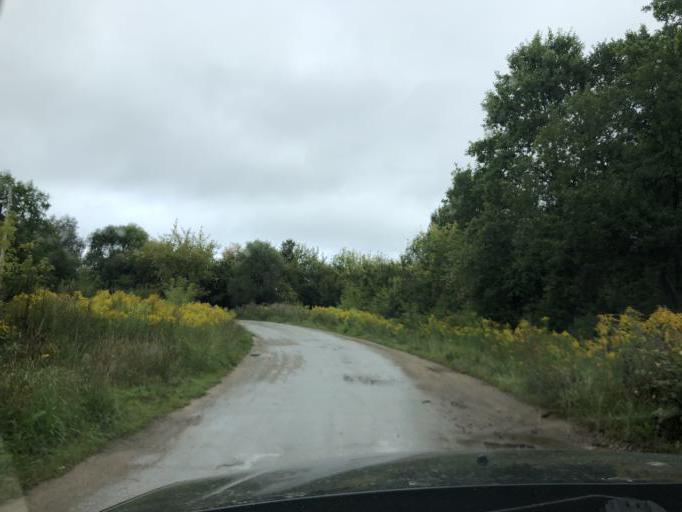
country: RU
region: Tula
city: Mendeleyevskiy
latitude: 54.1716
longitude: 37.5530
